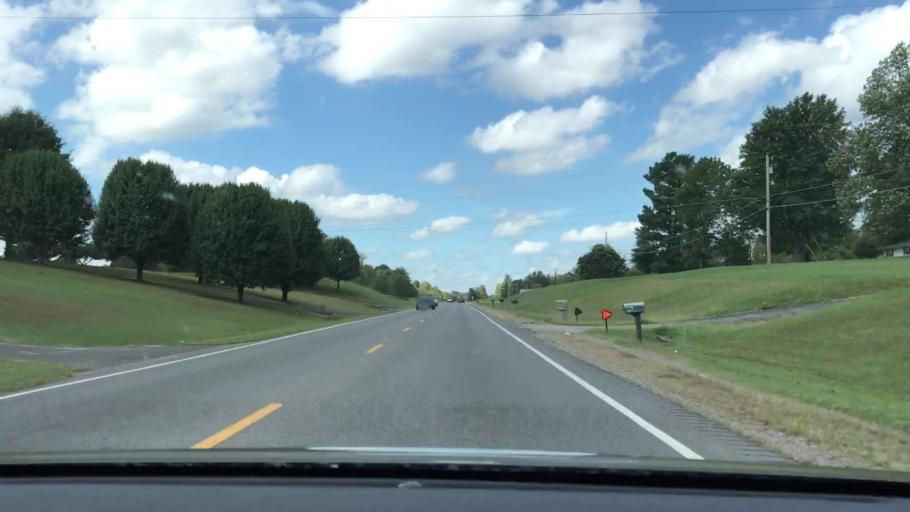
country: US
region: Kentucky
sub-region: Livingston County
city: Ledbetter
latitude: 37.0078
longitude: -88.4884
